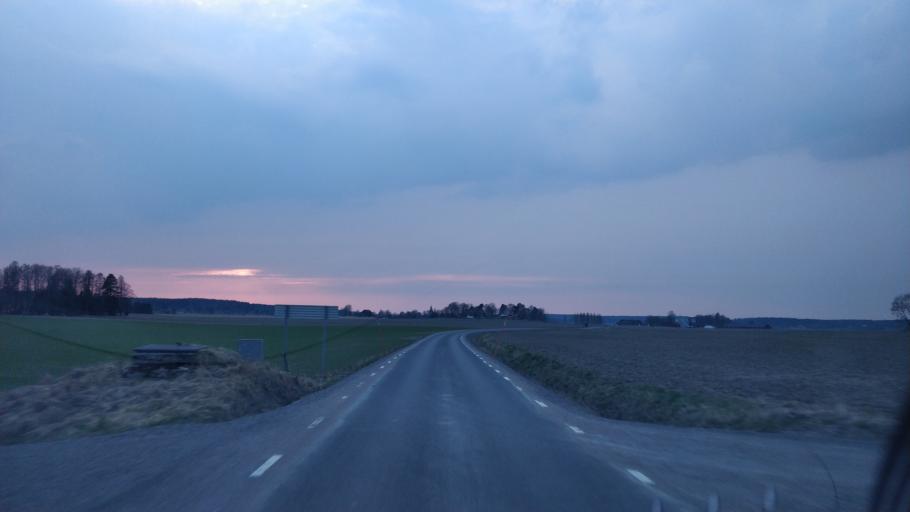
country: SE
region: Uppsala
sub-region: Enkopings Kommun
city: Orsundsbro
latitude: 59.7252
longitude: 17.2207
